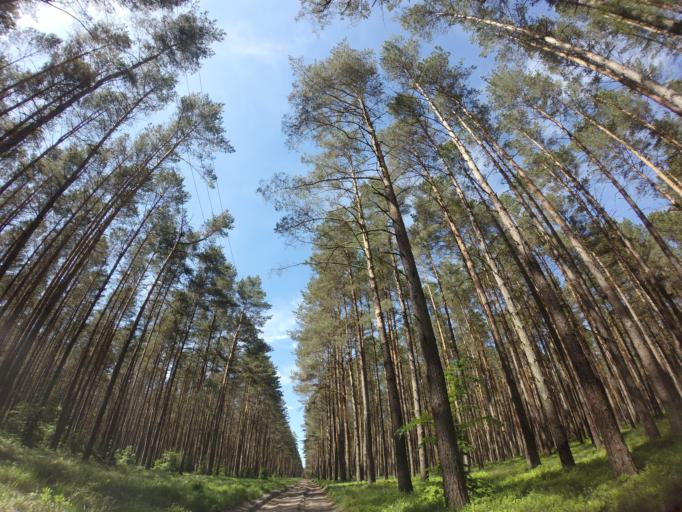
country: PL
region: West Pomeranian Voivodeship
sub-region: Powiat choszczenski
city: Drawno
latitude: 53.1237
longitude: 15.7999
